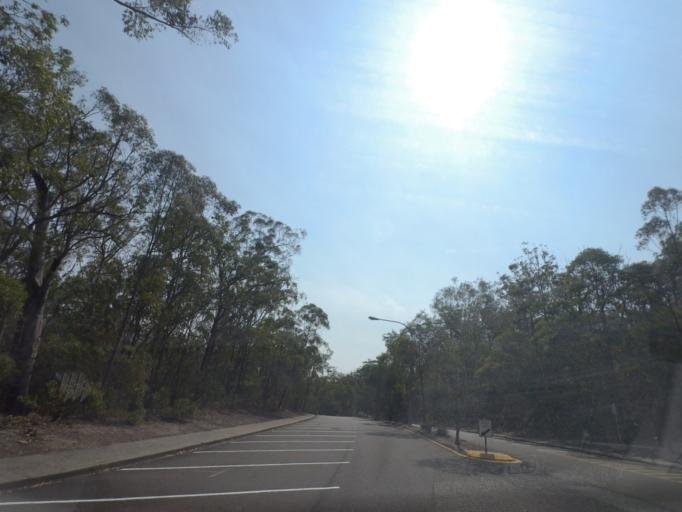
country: AU
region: Queensland
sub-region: Brisbane
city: Nathan
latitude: -27.5489
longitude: 153.0506
